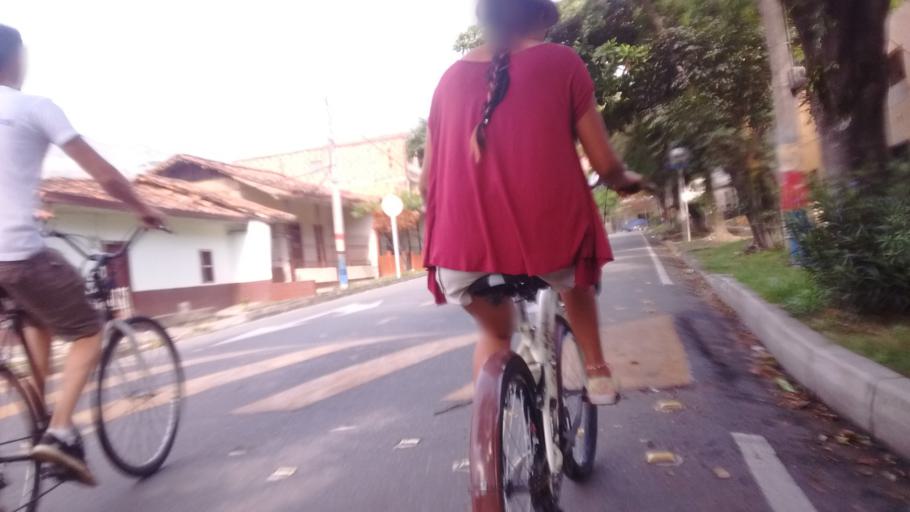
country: CO
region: Antioquia
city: Medellin
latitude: 6.2547
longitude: -75.6165
